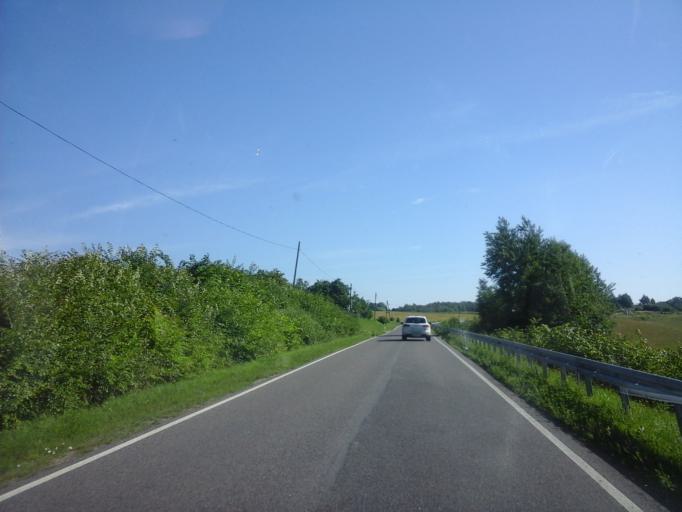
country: PL
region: West Pomeranian Voivodeship
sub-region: Powiat drawski
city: Zlocieniec
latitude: 53.6335
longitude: 15.9403
